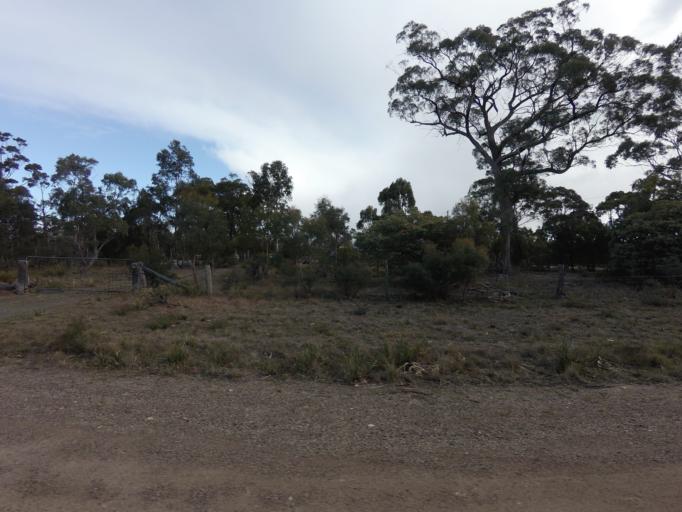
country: AU
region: Tasmania
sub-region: Sorell
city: Sorell
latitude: -42.3279
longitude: 147.9578
